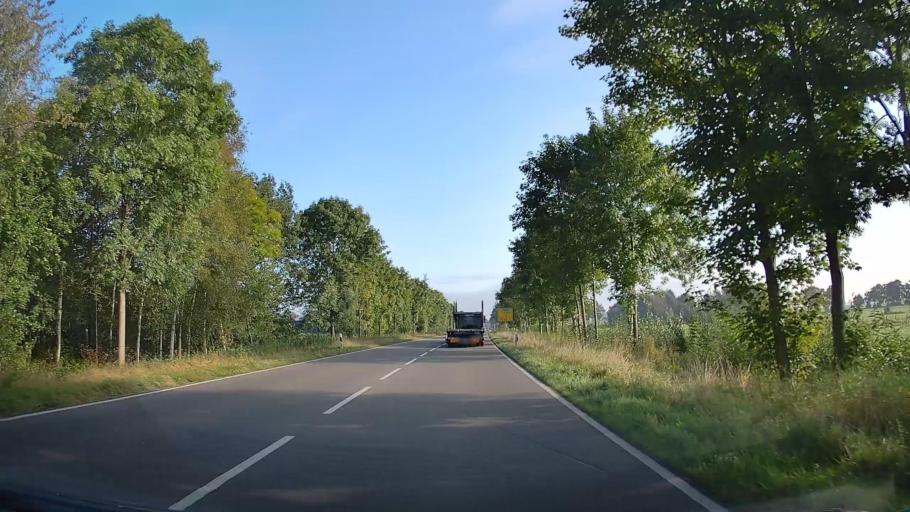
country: DE
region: Lower Saxony
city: Rastede
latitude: 53.2579
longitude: 8.3062
